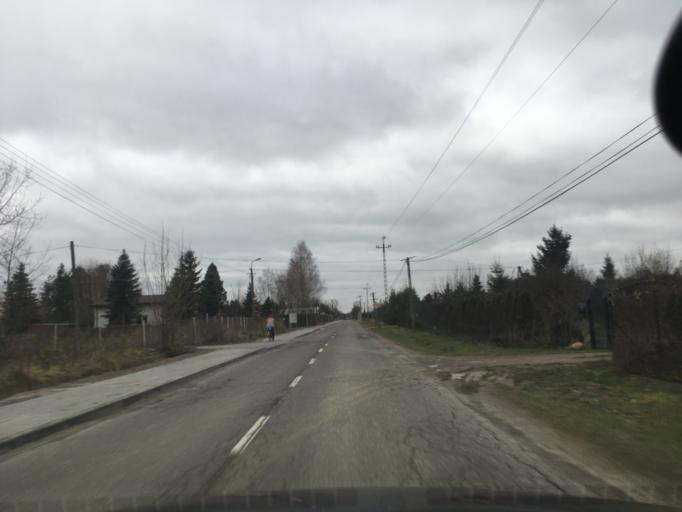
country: PL
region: Masovian Voivodeship
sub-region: Powiat piaseczynski
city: Lesznowola
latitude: 52.0434
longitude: 20.9531
